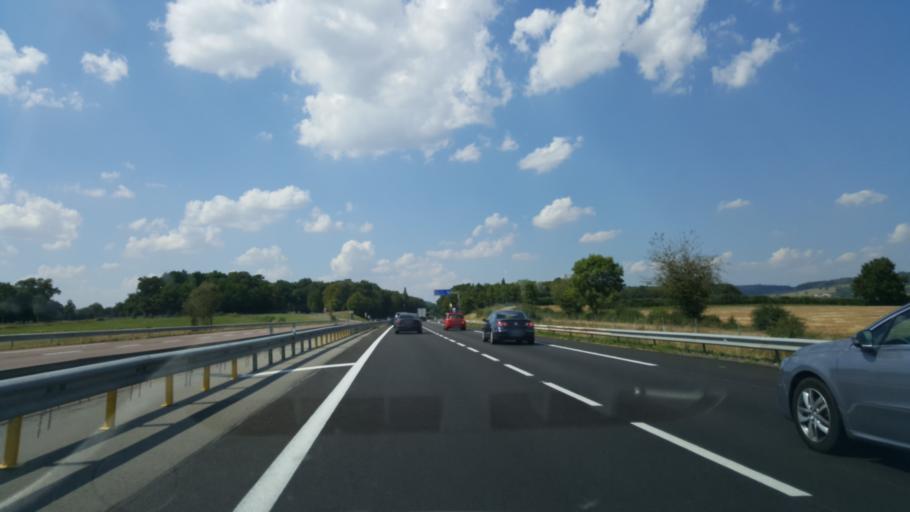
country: FR
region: Bourgogne
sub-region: Departement de la Cote-d'Or
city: Pouilly-en-Auxois
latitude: 47.2185
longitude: 4.5986
